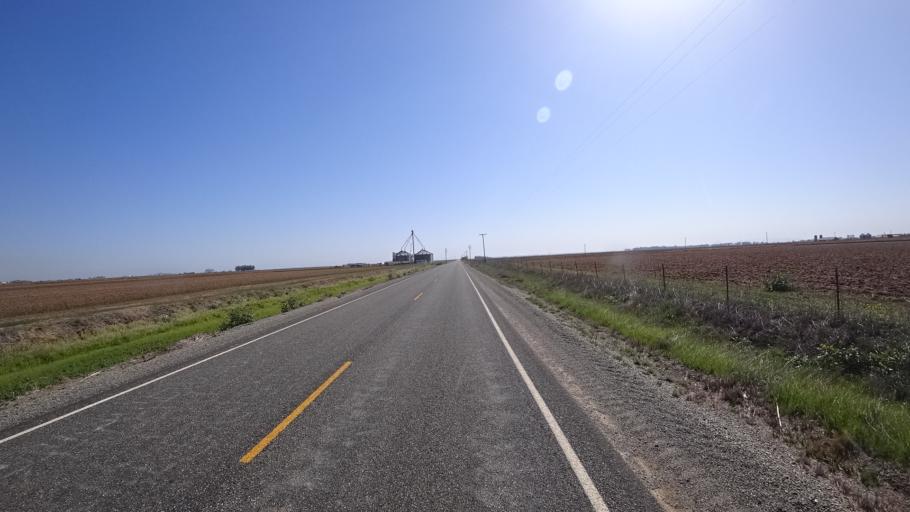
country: US
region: California
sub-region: Glenn County
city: Willows
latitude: 39.4656
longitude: -122.1585
